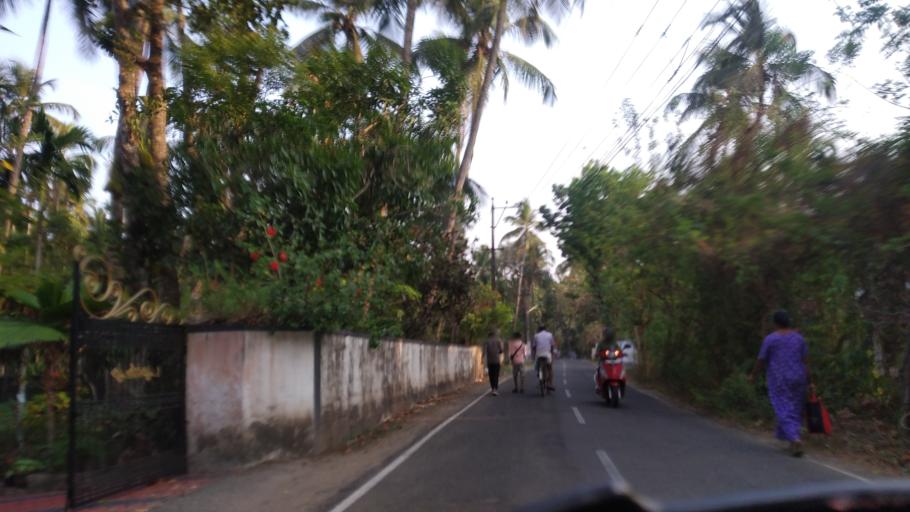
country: IN
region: Kerala
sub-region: Thrissur District
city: Thanniyam
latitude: 10.4081
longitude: 76.0947
